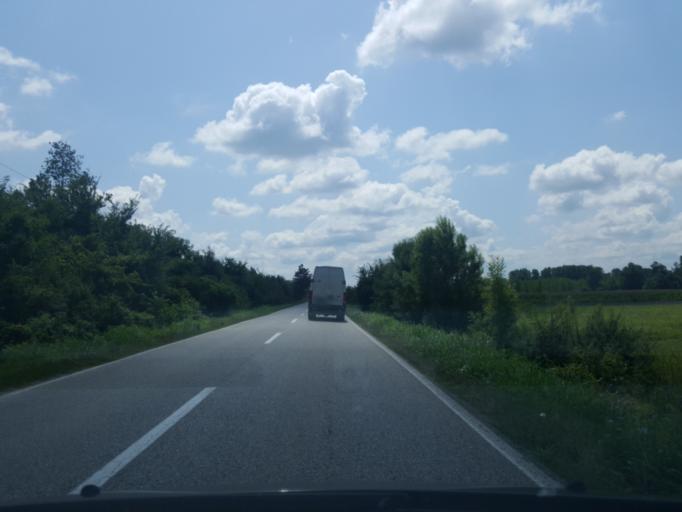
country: RS
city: Glusci
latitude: 44.9195
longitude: 19.5431
